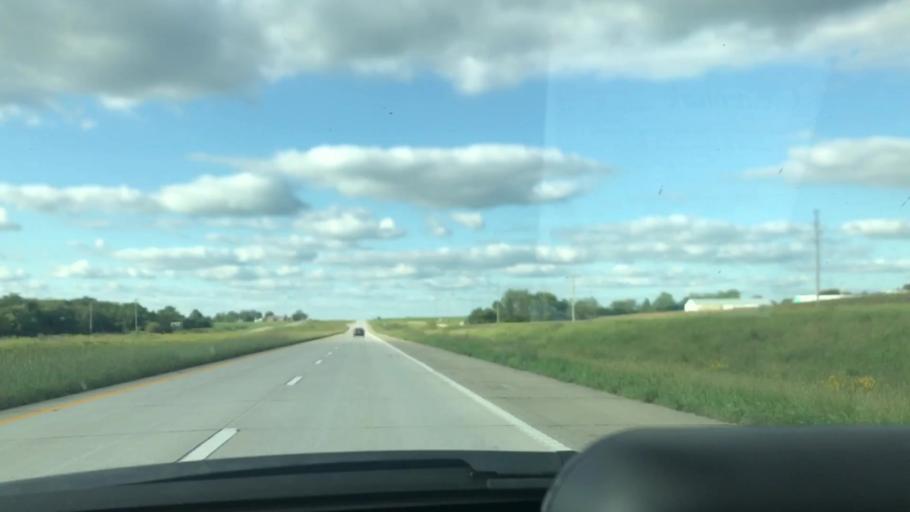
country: US
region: Missouri
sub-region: Benton County
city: Cole Camp
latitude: 38.4930
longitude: -93.2735
